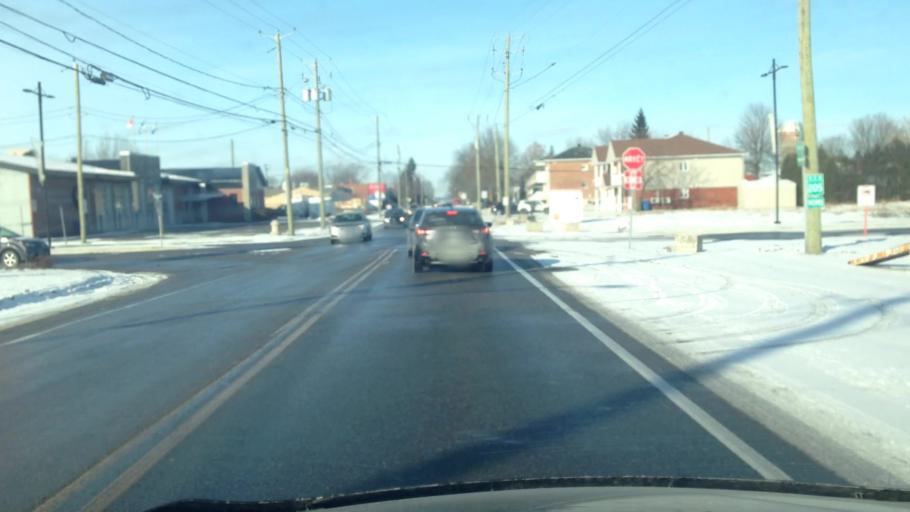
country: CA
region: Quebec
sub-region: Monteregie
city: Beauharnois
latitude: 45.3077
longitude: -73.8606
